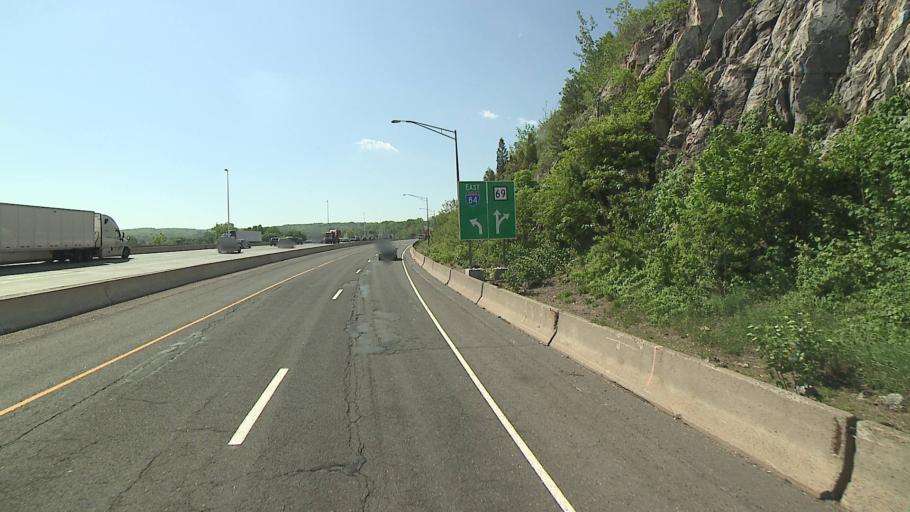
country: US
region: Connecticut
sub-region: New Haven County
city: Waterbury
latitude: 41.5484
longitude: -73.0281
